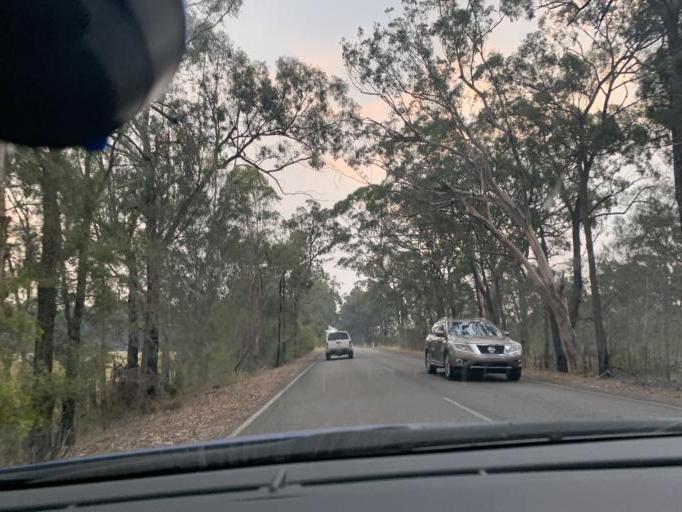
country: AU
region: New South Wales
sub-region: Cessnock
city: Cessnock
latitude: -32.9205
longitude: 151.3440
